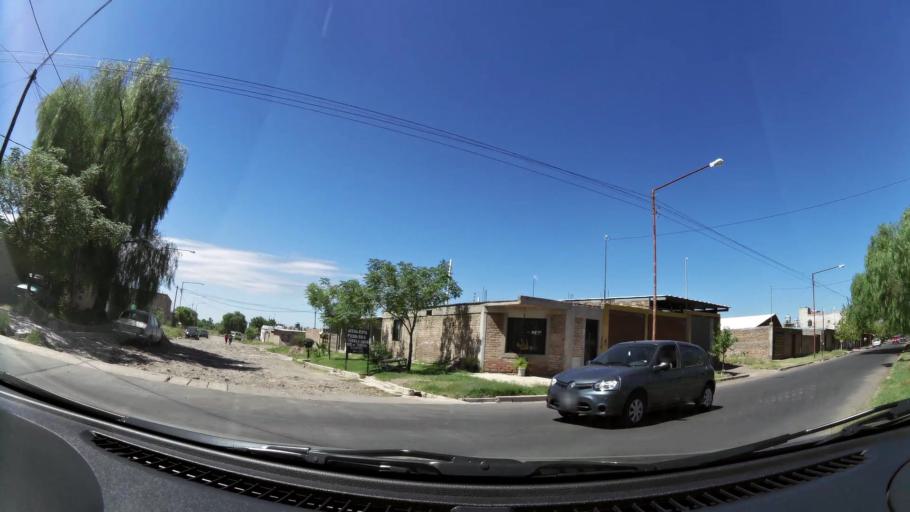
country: AR
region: Mendoza
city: Las Heras
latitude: -32.8415
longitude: -68.8643
